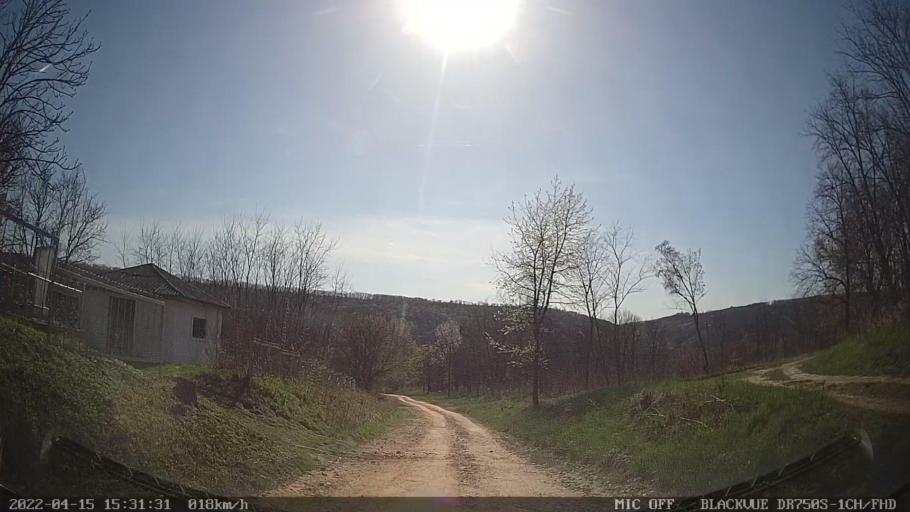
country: MD
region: Raionul Ocnita
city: Otaci
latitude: 48.3525
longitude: 27.9203
